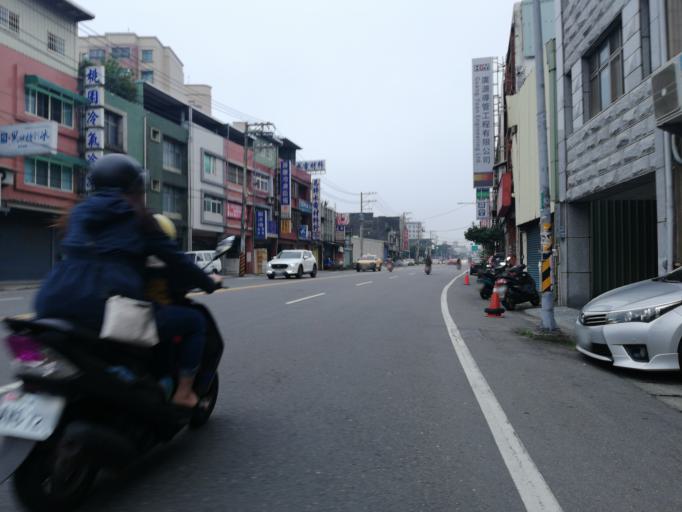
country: TW
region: Taiwan
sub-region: Taoyuan
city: Taoyuan
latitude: 24.9840
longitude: 121.3101
